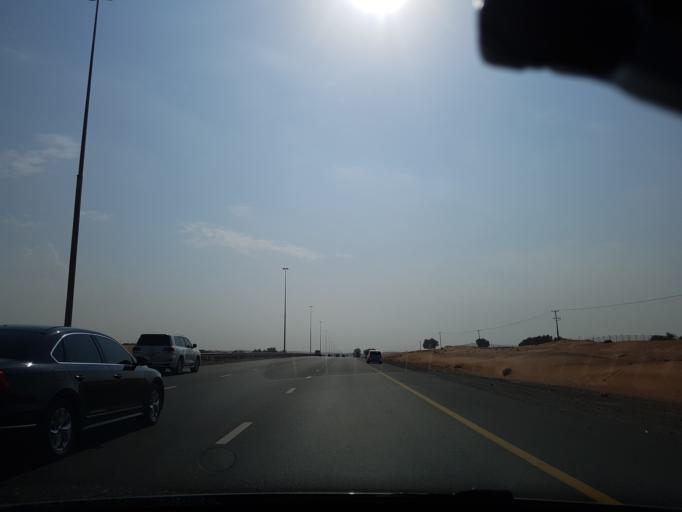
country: AE
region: Umm al Qaywayn
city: Umm al Qaywayn
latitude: 25.5207
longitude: 55.7147
